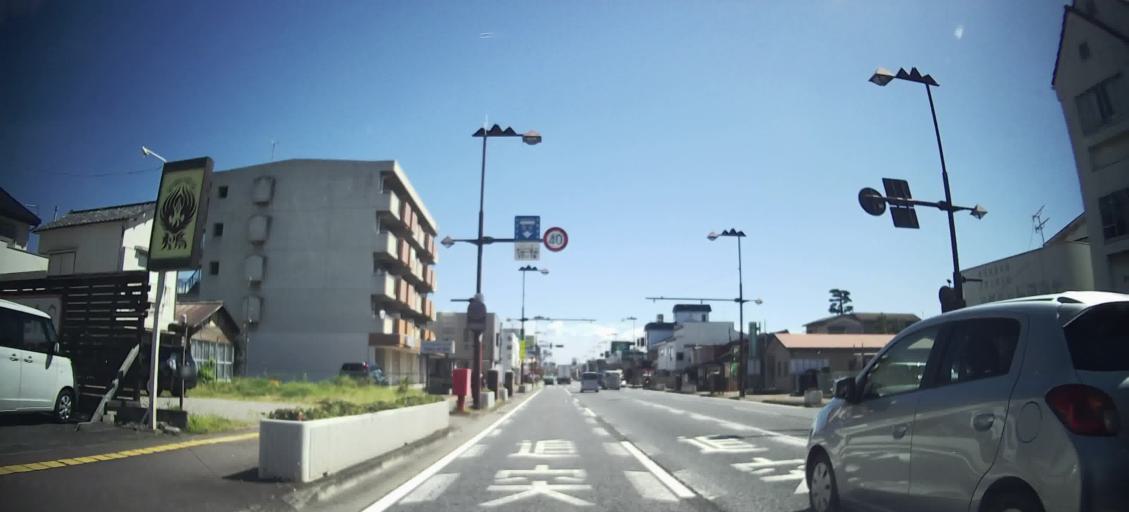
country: JP
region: Gunma
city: Maebashi-shi
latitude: 36.3847
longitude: 139.0833
